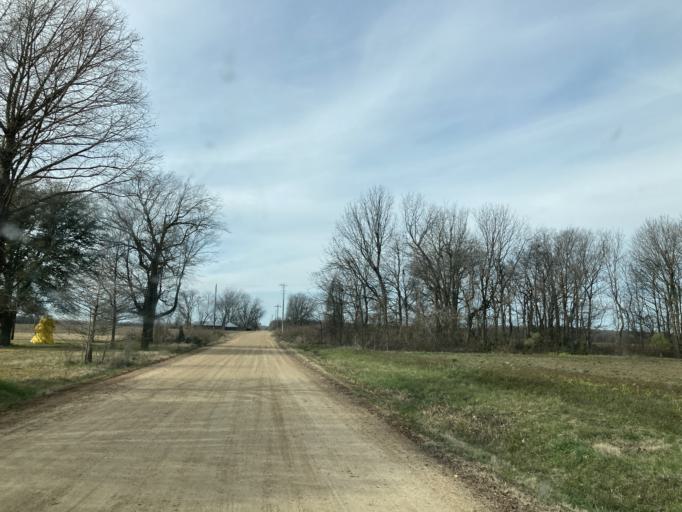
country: US
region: Mississippi
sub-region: Humphreys County
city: Belzoni
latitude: 33.1383
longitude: -90.6074
